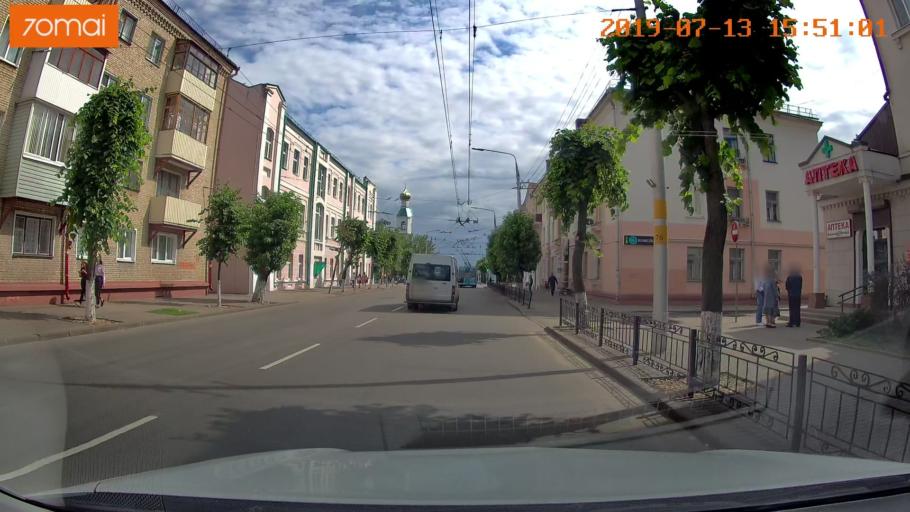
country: BY
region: Mogilev
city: Babruysk
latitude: 53.1406
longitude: 29.2244
